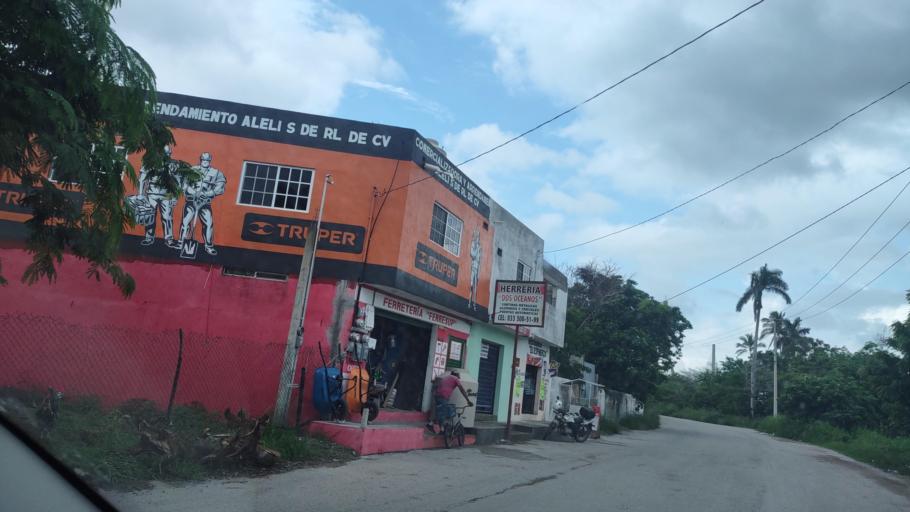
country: MX
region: Veracruz
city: Anahuac
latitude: 22.2249
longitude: -97.8300
